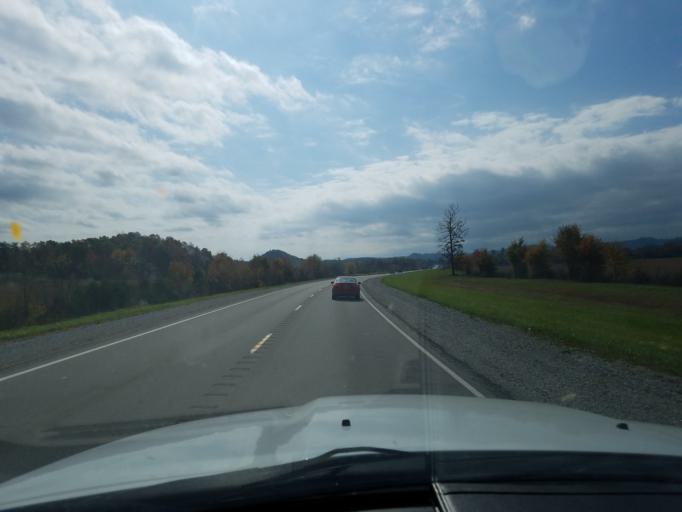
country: US
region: Kentucky
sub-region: Marion County
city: Lebanon
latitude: 37.4999
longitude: -85.2926
